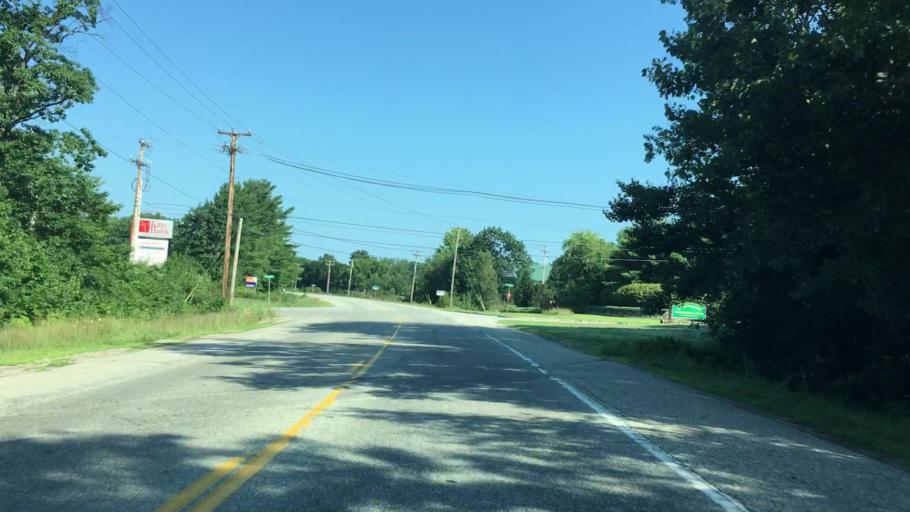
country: US
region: Maine
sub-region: Androscoggin County
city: Minot
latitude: 44.0373
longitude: -70.2745
